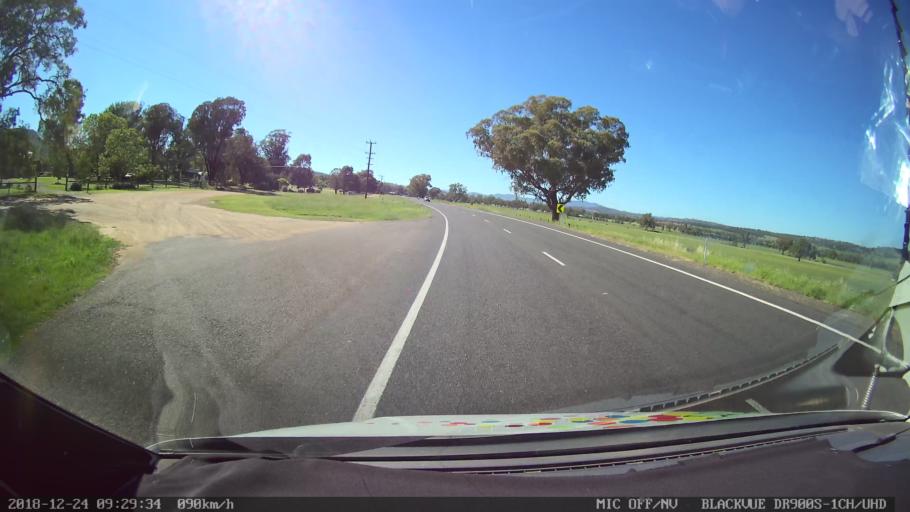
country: AU
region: New South Wales
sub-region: Liverpool Plains
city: Quirindi
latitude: -31.5527
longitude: 150.6924
